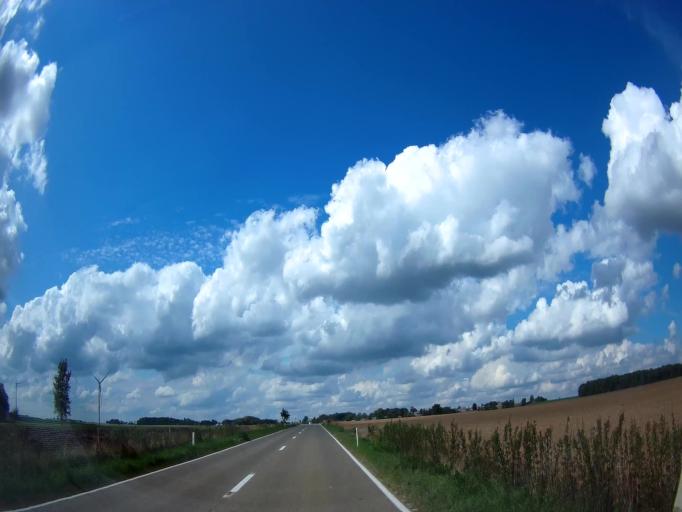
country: BE
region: Wallonia
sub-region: Province de Namur
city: Ohey
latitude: 50.4216
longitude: 5.1393
